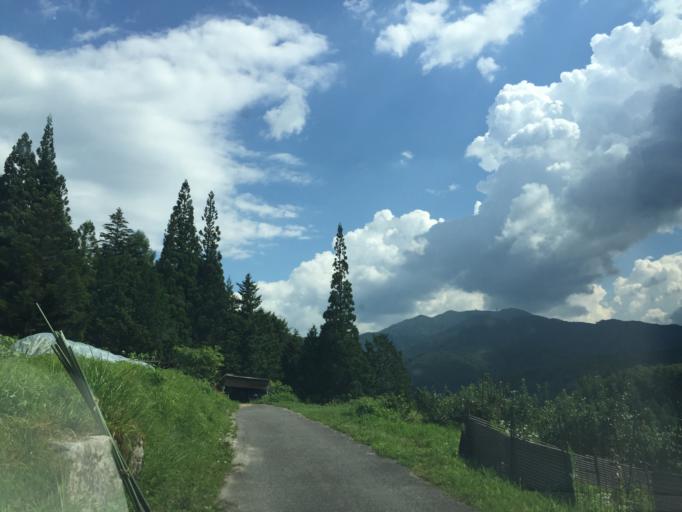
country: JP
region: Nagano
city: Iida
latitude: 35.3856
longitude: 137.6862
